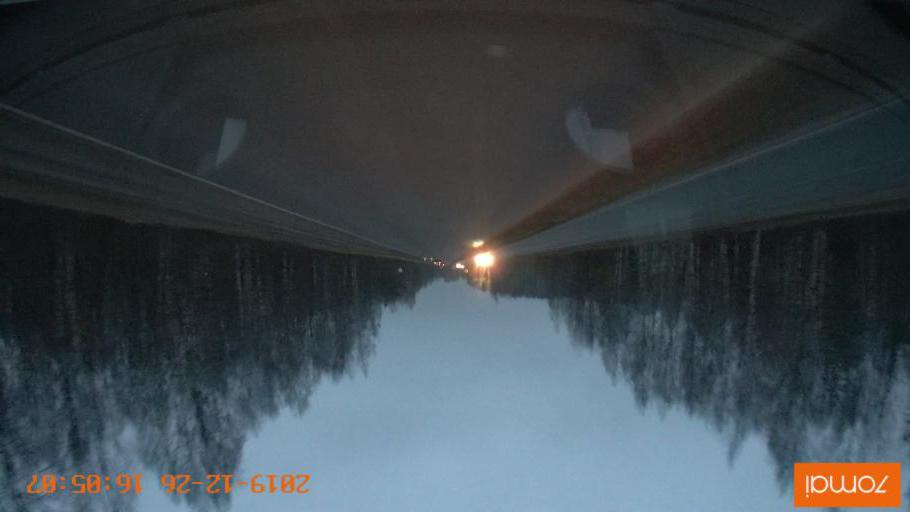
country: RU
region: Jaroslavl
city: Rybinsk
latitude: 58.0070
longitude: 38.8874
